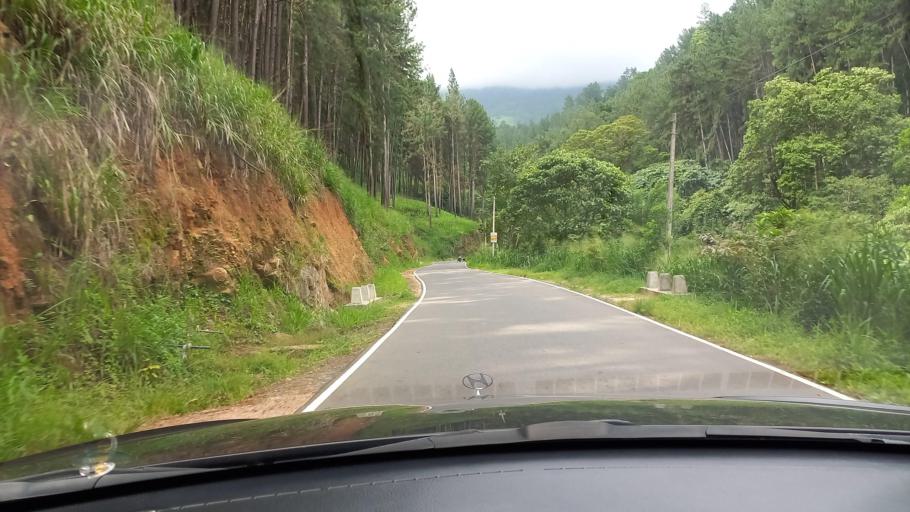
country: LK
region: Central
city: Gampola
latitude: 7.2128
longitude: 80.6192
